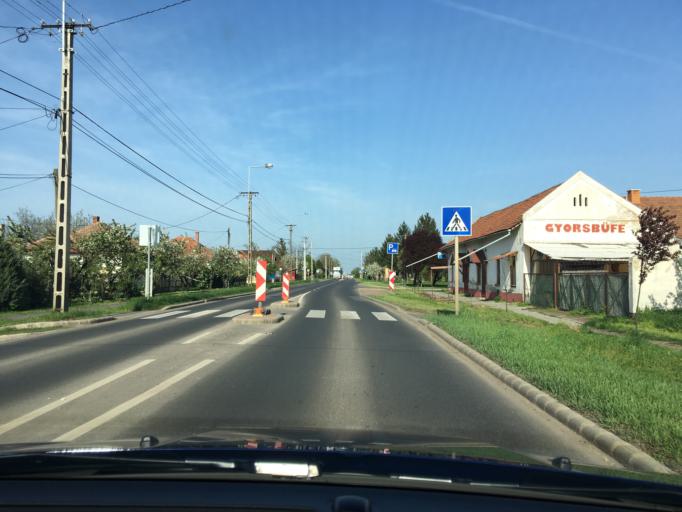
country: HU
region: Bekes
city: Csorvas
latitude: 46.6360
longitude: 20.8370
